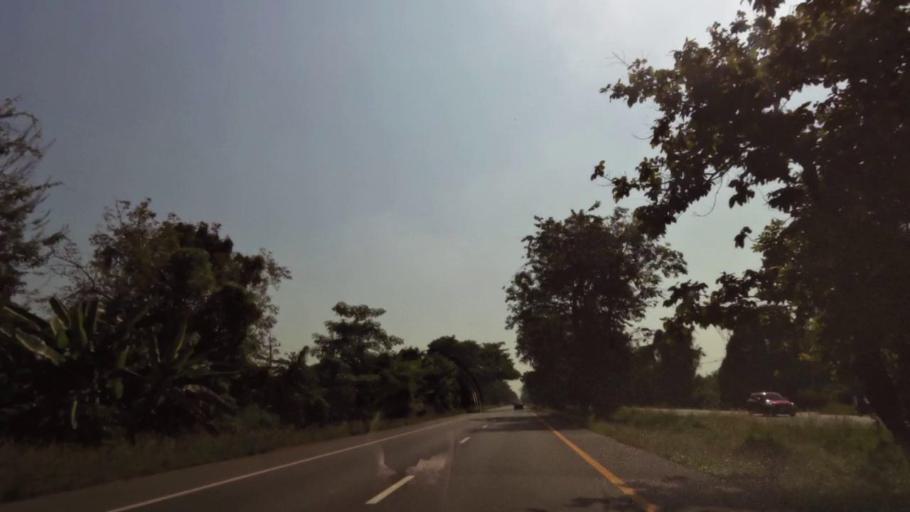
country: TH
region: Nakhon Sawan
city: Banphot Phisai
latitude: 16.0028
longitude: 100.1160
